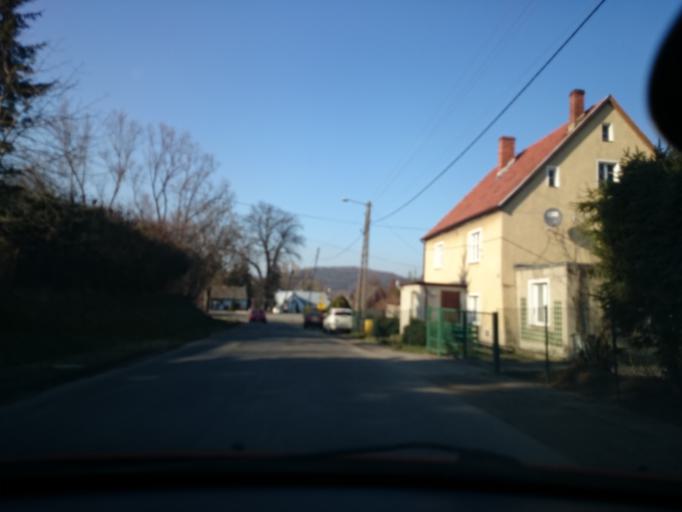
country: PL
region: Lower Silesian Voivodeship
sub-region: Powiat klodzki
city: Klodzko
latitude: 50.3854
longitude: 16.6285
